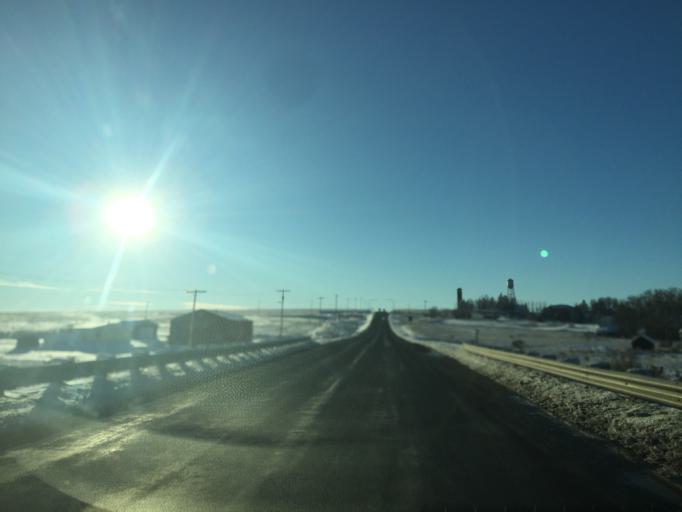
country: US
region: Washington
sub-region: Okanogan County
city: Coulee Dam
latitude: 47.7082
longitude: -118.9327
